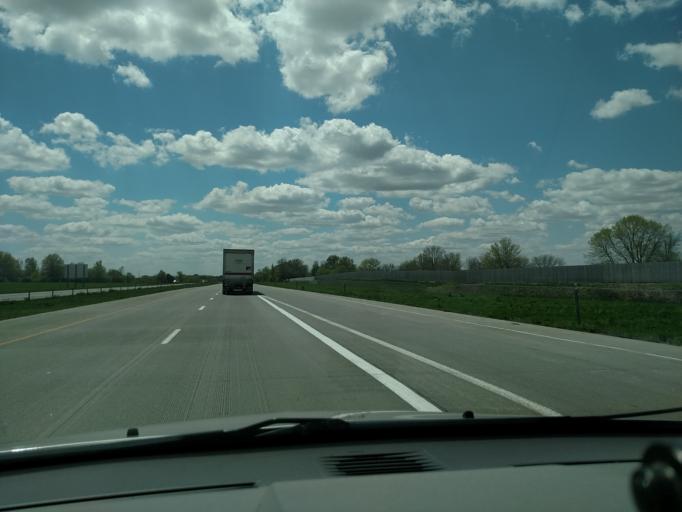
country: US
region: Iowa
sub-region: Polk County
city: Ankeny
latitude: 41.7546
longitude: -93.5719
